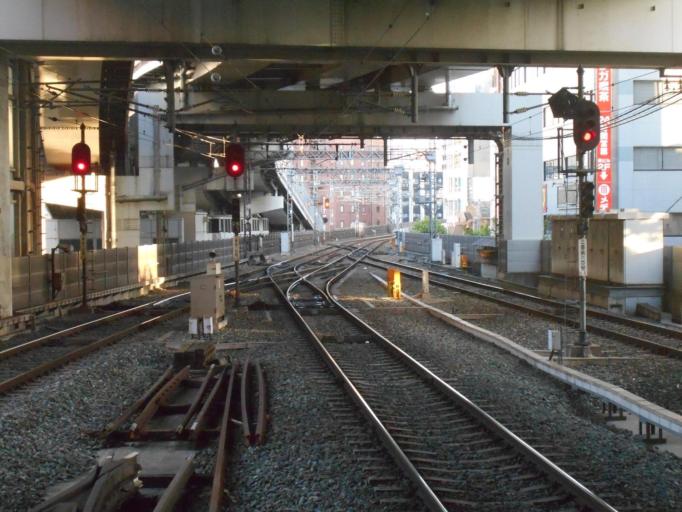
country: JP
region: Fukuoka
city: Fukuoka-shi
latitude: 33.5877
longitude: 130.4007
